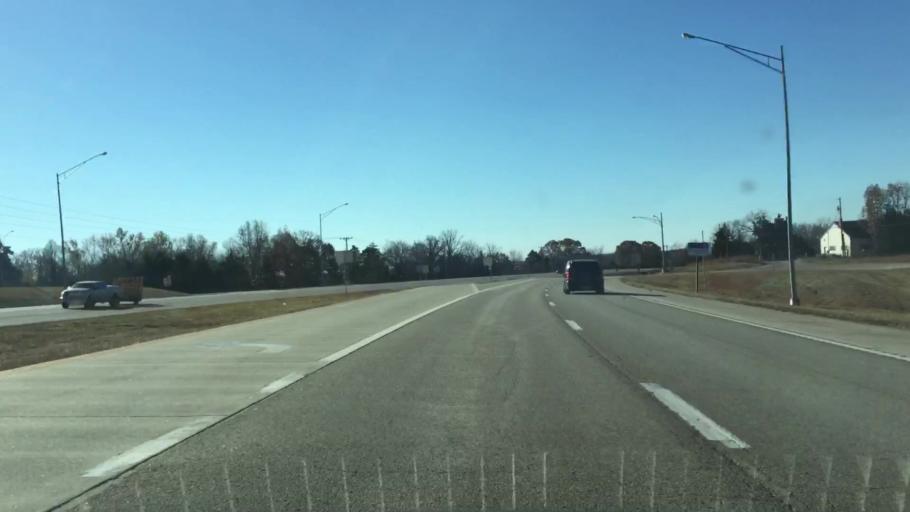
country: US
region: Missouri
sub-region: Cole County
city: Wardsville
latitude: 38.4417
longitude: -92.3037
